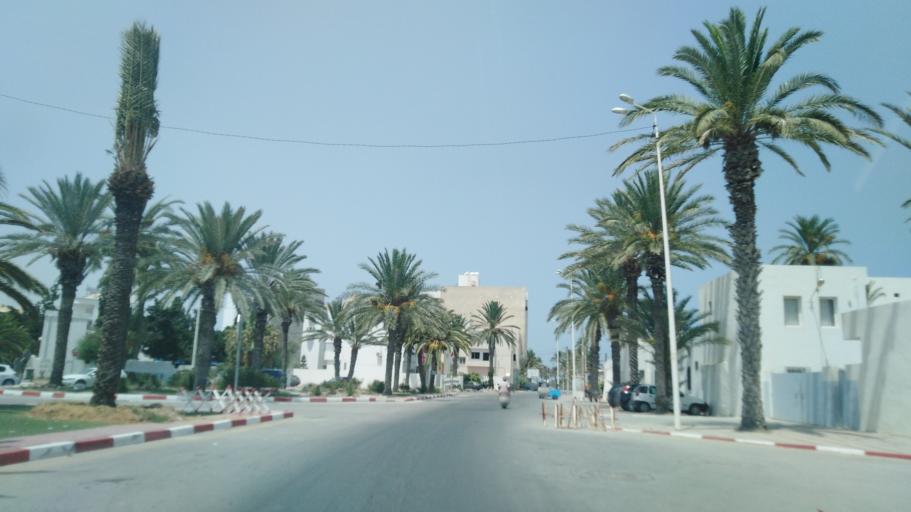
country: TN
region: Al Mahdiyah
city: Mahdia
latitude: 35.5173
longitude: 11.0438
